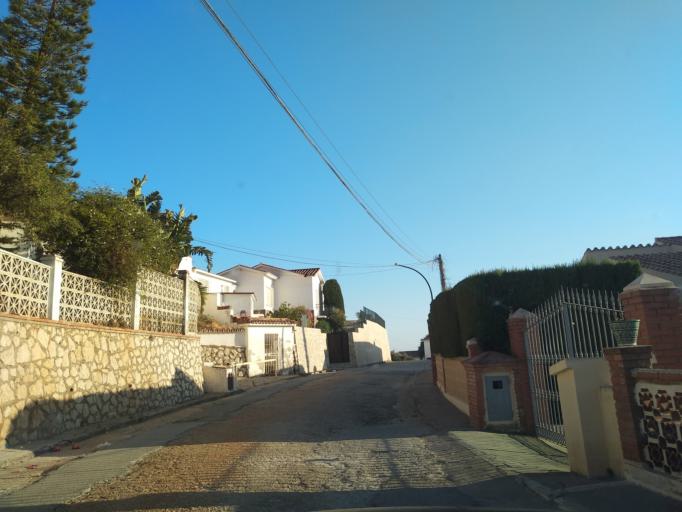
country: ES
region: Andalusia
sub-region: Provincia de Malaga
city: Valdes
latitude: 36.7186
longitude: -4.1917
